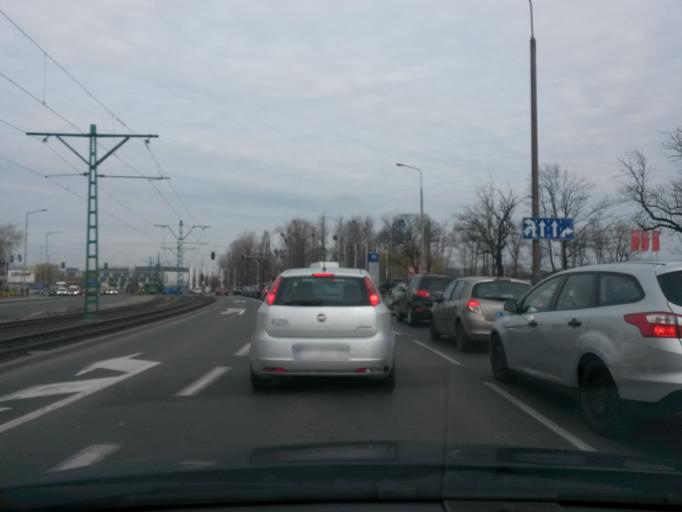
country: PL
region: Greater Poland Voivodeship
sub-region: Poznan
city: Poznan
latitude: 52.4027
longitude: 16.9546
